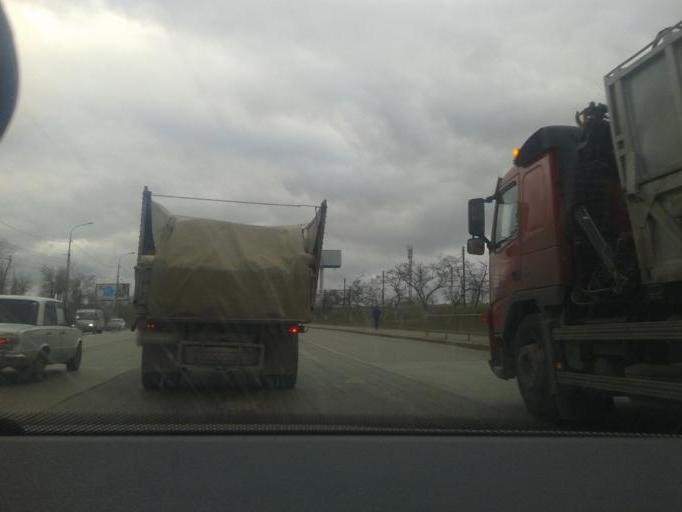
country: RU
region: Volgograd
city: Volgograd
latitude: 48.6667
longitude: 44.4410
